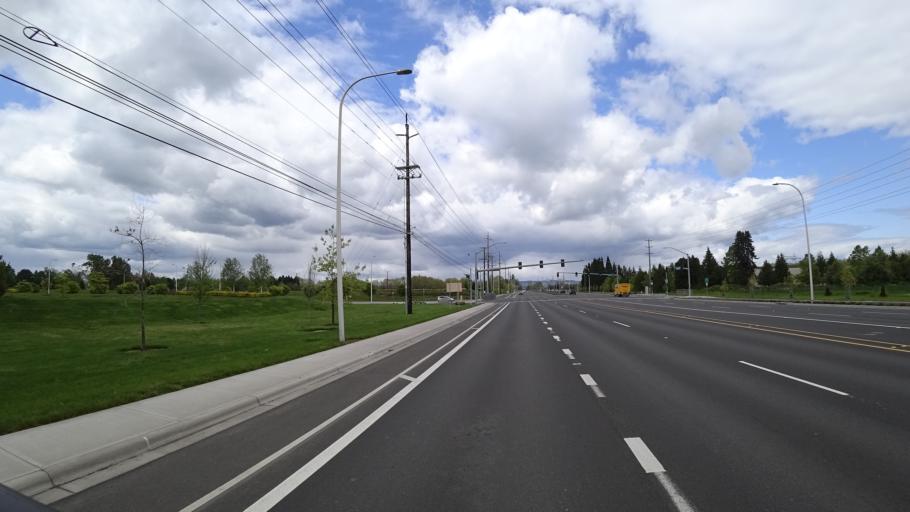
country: US
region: Oregon
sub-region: Washington County
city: Rockcreek
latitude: 45.5425
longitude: -122.9002
